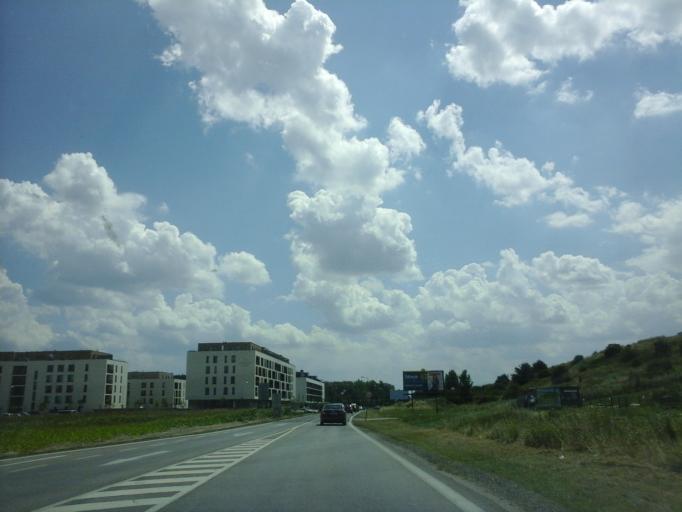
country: AT
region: Burgenland
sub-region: Politischer Bezirk Neusiedl am See
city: Kittsee
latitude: 48.0894
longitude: 17.1228
